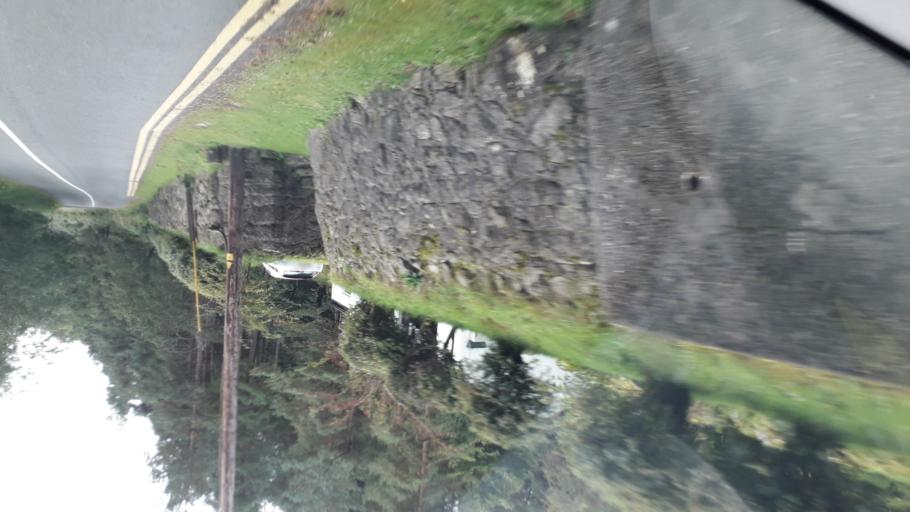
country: IE
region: Leinster
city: Ballyboden
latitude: 53.2426
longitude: -6.2938
